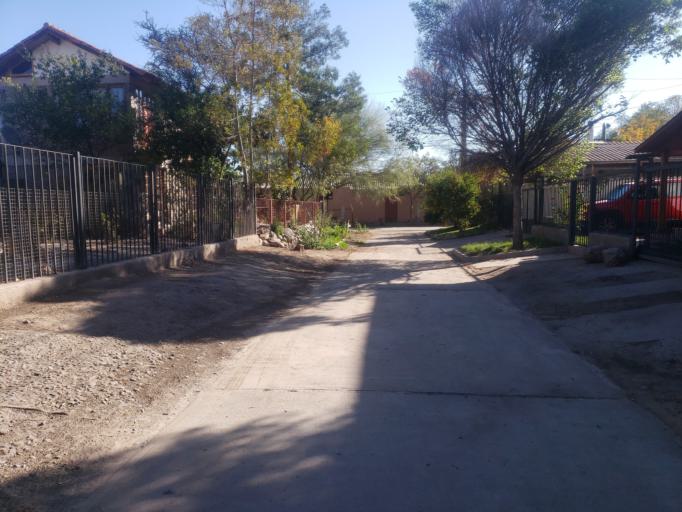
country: CL
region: Valparaiso
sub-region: Provincia de Los Andes
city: Los Andes
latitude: -32.8329
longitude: -70.6133
